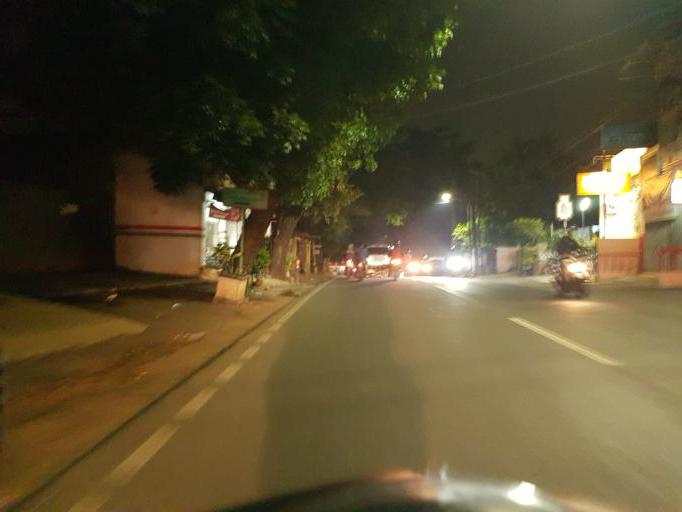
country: ID
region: West Java
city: Cileungsir
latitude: -6.3141
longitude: 106.9093
